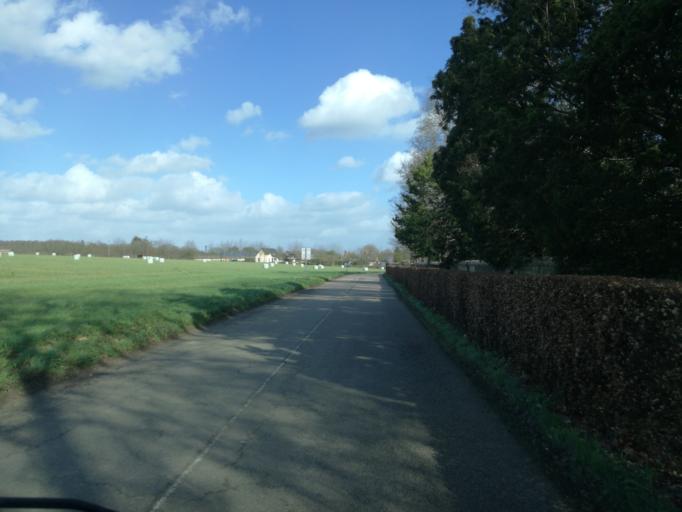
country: FR
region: Haute-Normandie
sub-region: Departement de la Seine-Maritime
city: Sahurs
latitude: 49.3589
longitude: 0.9687
